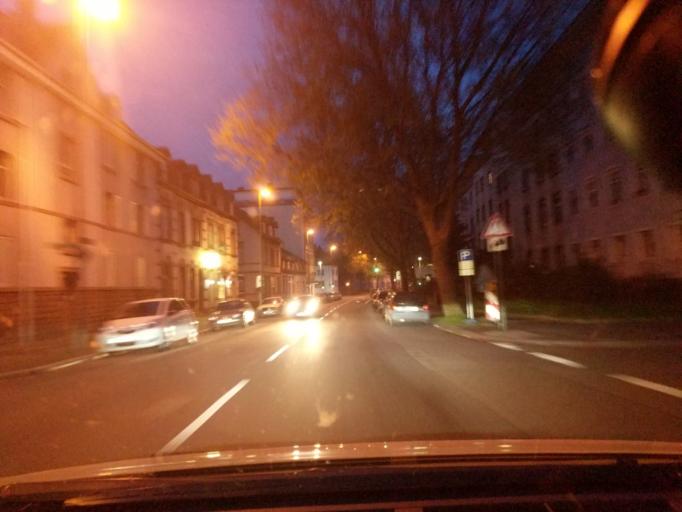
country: DE
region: Rheinland-Pfalz
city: Kaiserslautern
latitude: 49.4485
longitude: 7.7822
